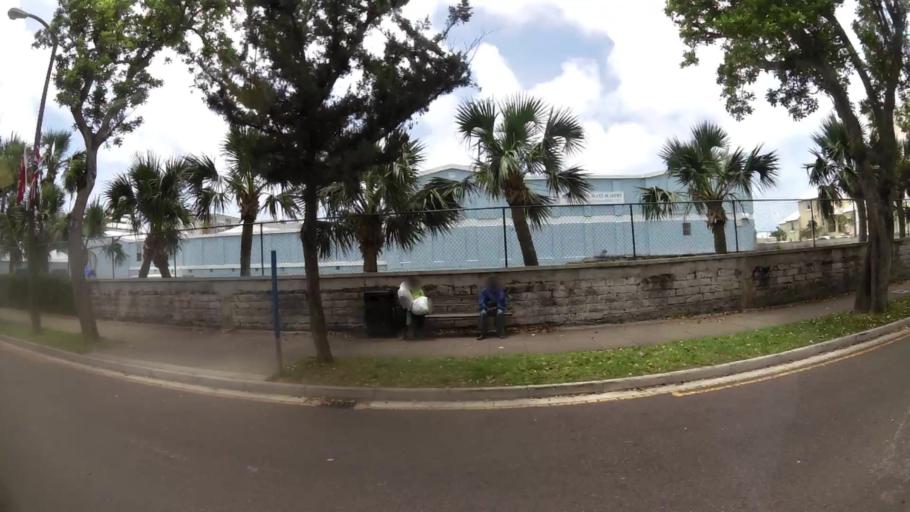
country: BM
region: Hamilton city
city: Hamilton
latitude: 32.2966
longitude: -64.7844
